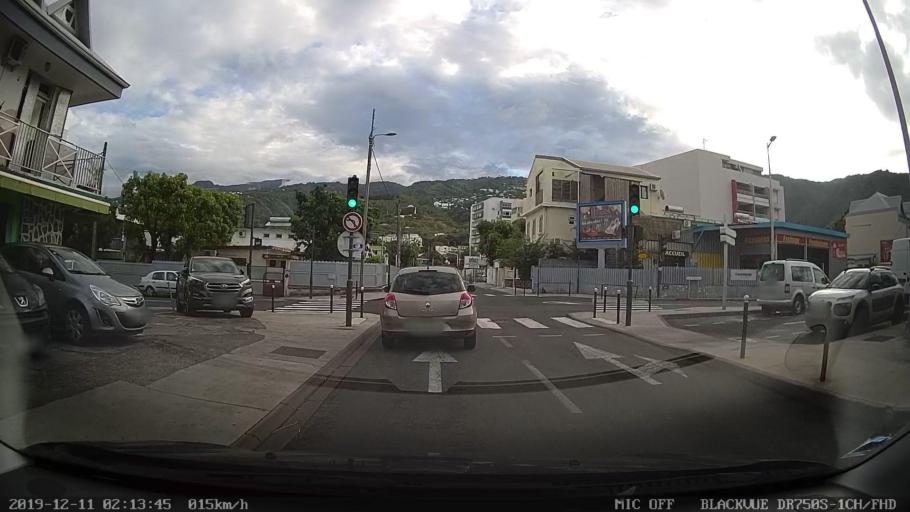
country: RE
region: Reunion
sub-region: Reunion
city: Saint-Denis
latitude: -20.8889
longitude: 55.4533
